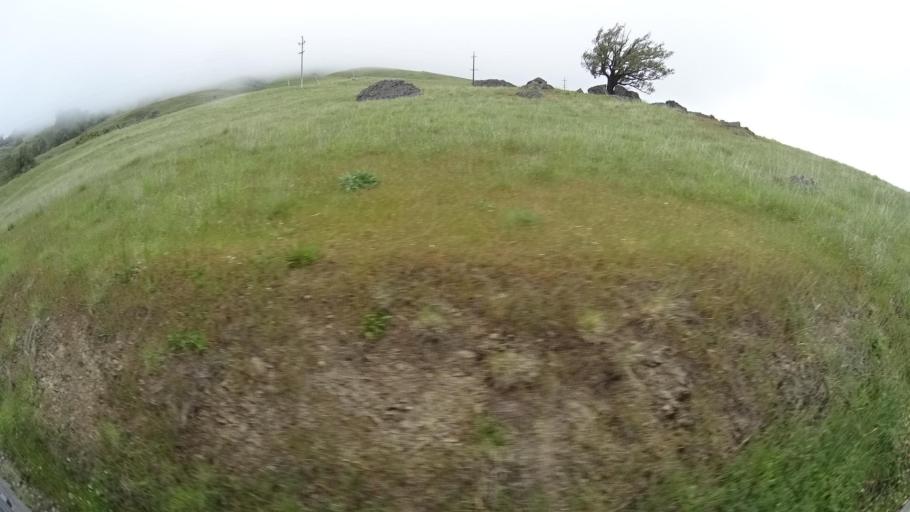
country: US
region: California
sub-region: Humboldt County
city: Redway
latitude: 40.1058
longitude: -123.7147
